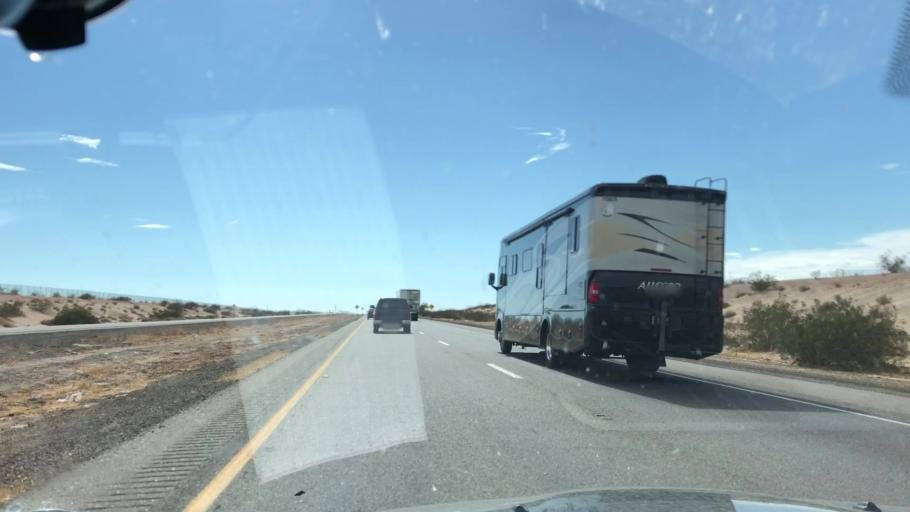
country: US
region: California
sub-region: Riverside County
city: Mesa Verde
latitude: 33.6070
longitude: -114.7046
